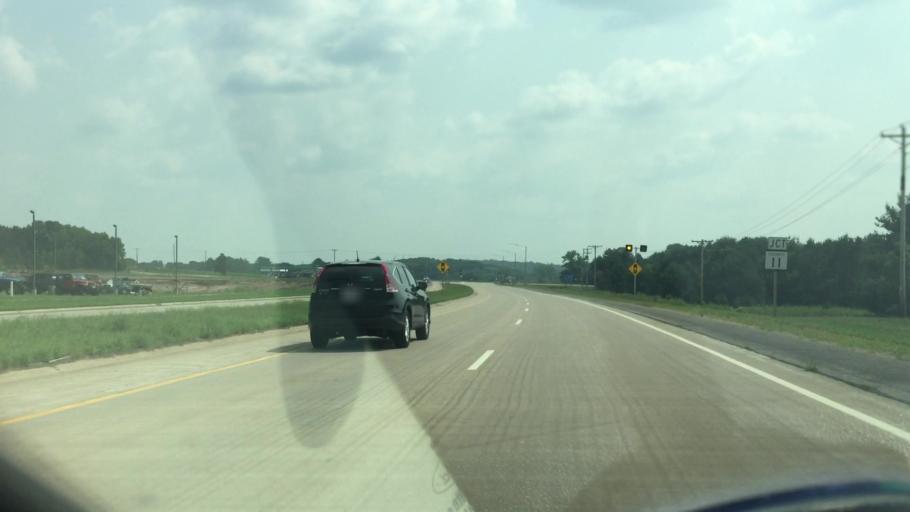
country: US
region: Wisconsin
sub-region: Eau Claire County
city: Altoona
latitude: 44.7446
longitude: -91.4507
